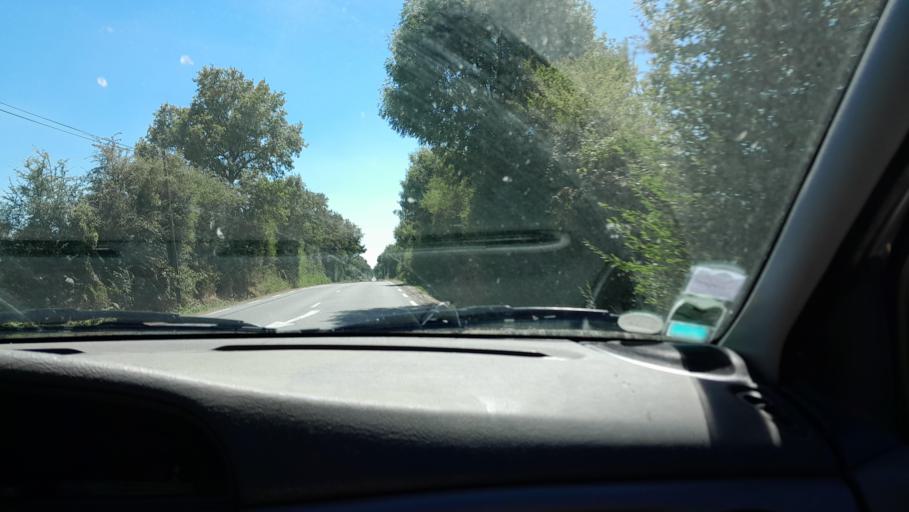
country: FR
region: Pays de la Loire
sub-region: Departement de Maine-et-Loire
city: Pouance
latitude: 47.6691
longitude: -1.1892
